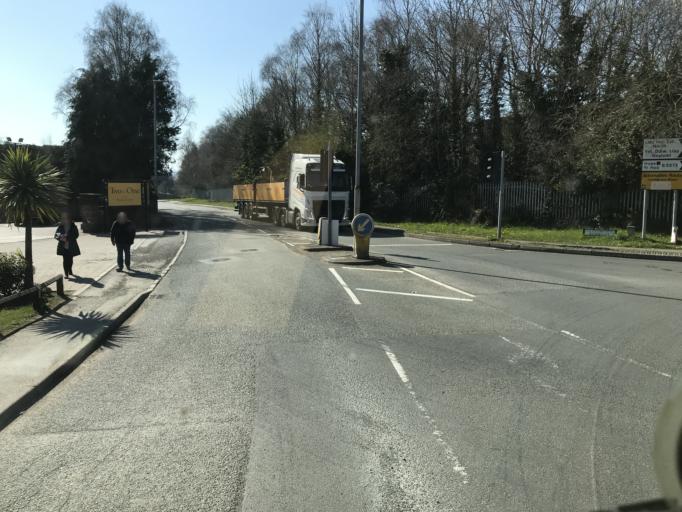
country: GB
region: Wales
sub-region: Wrexham
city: Gresford
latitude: 53.0999
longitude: -2.9980
